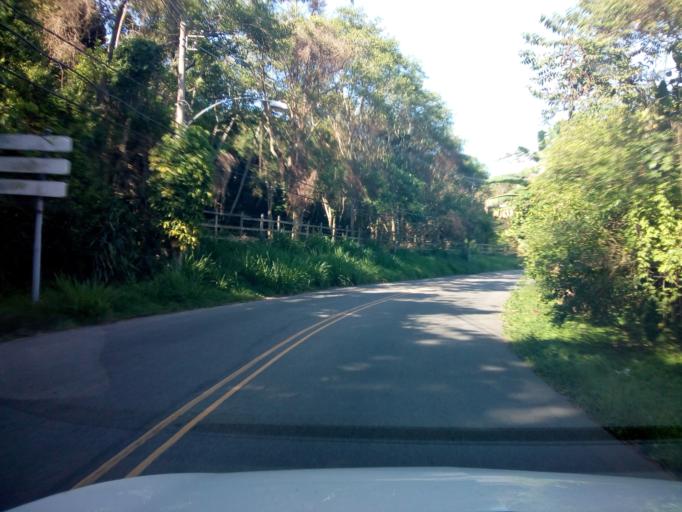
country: BR
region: Rio de Janeiro
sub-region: Nilopolis
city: Nilopolis
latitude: -23.0255
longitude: -43.5103
